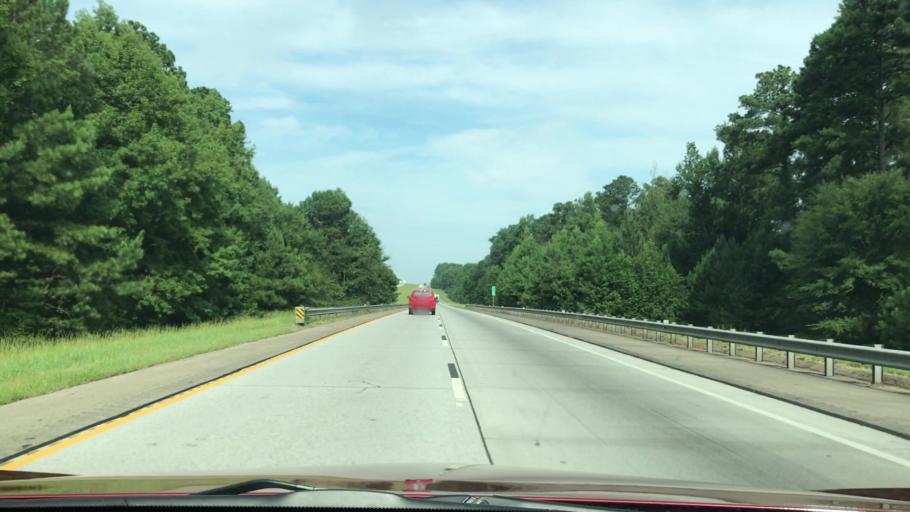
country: US
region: Georgia
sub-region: Columbia County
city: Appling
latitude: 33.5045
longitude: -82.3805
